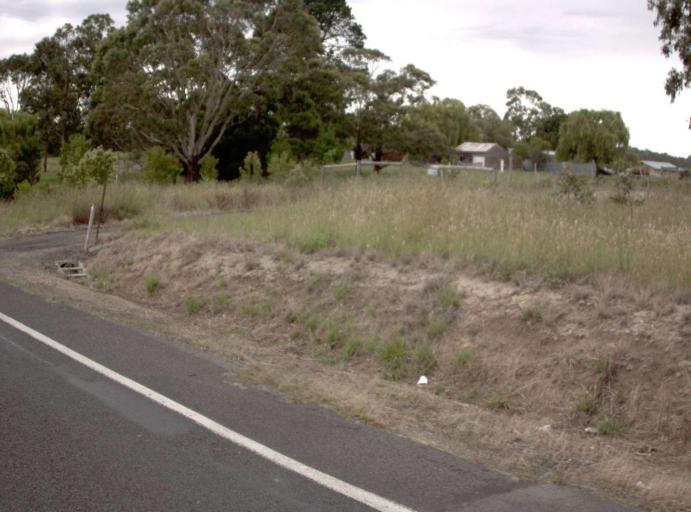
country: AU
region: Victoria
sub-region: Wellington
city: Sale
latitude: -38.2974
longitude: 147.0340
